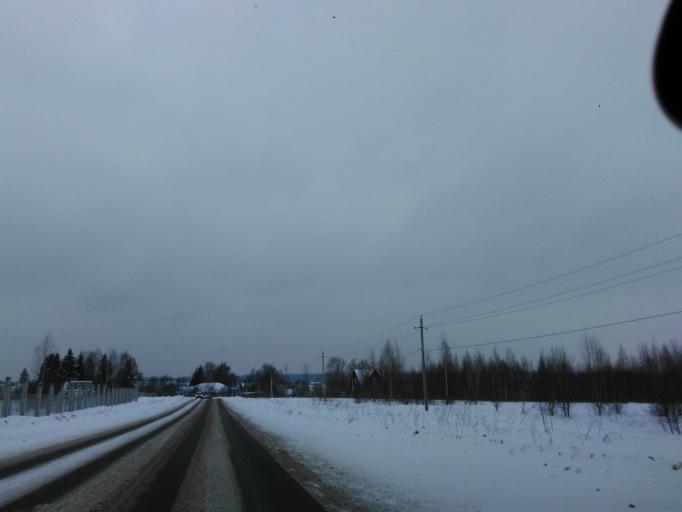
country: RU
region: Moskovskaya
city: Yakhroma
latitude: 56.2697
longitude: 37.4605
